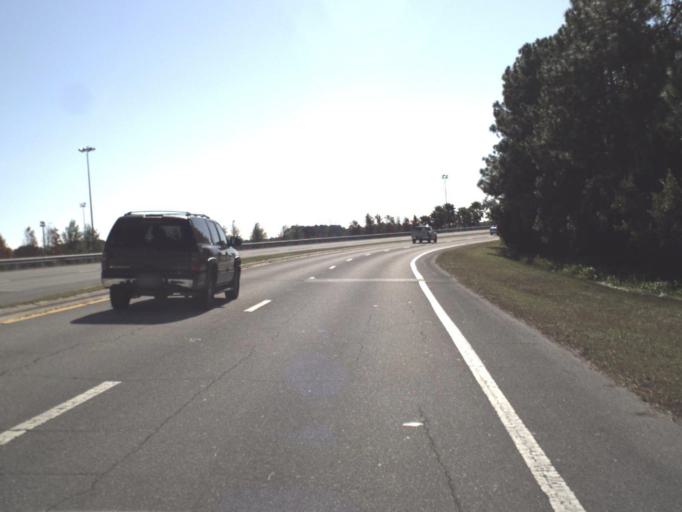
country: US
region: Florida
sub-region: Volusia County
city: Daytona Beach
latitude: 29.1793
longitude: -81.0770
